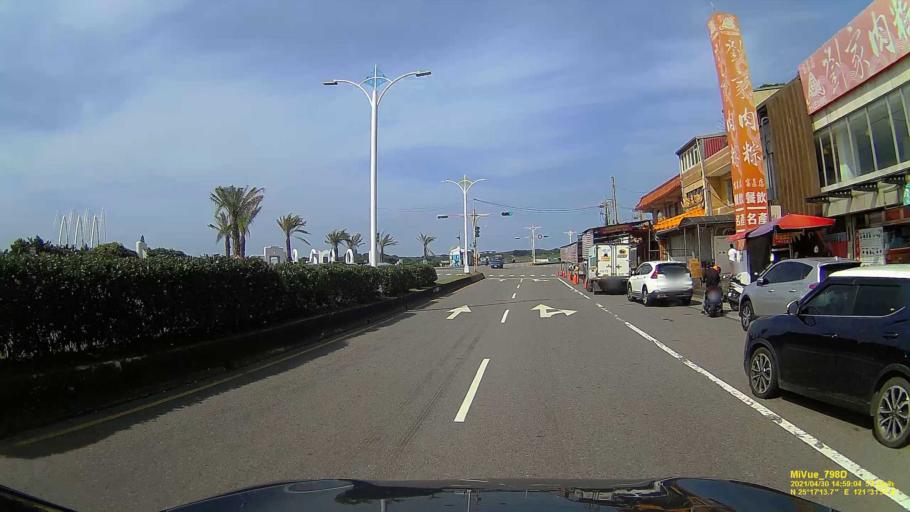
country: TW
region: Taipei
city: Taipei
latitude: 25.2874
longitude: 121.5312
